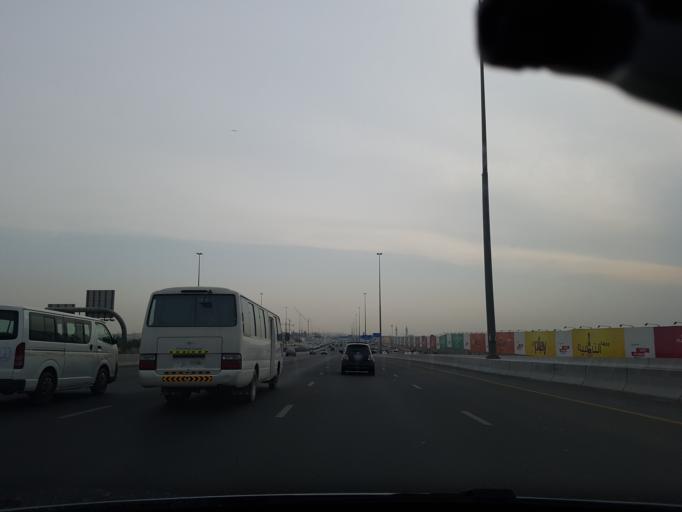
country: AE
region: Ash Shariqah
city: Sharjah
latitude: 25.3327
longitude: 55.4637
